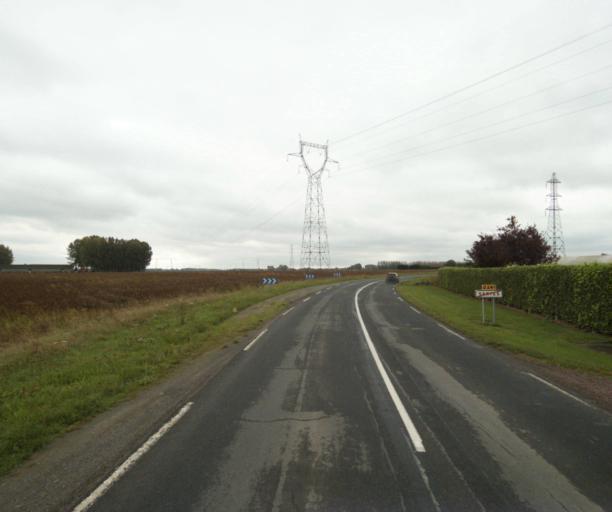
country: FR
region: Nord-Pas-de-Calais
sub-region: Departement du Nord
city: Santes
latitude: 50.5899
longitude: 2.9477
